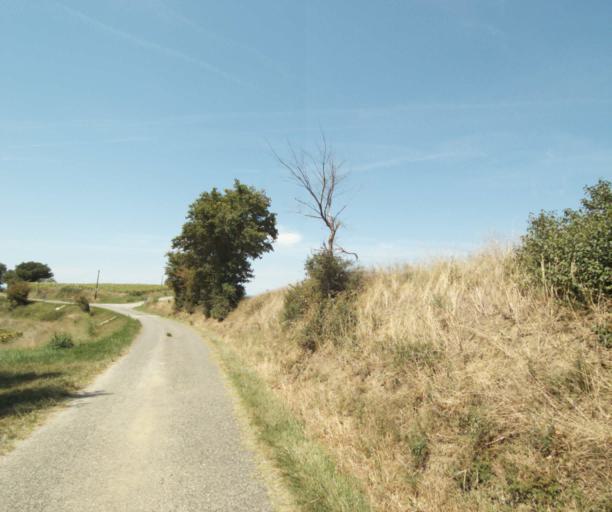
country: FR
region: Midi-Pyrenees
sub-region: Departement de l'Ariege
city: Lezat-sur-Leze
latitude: 43.3088
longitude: 1.3712
